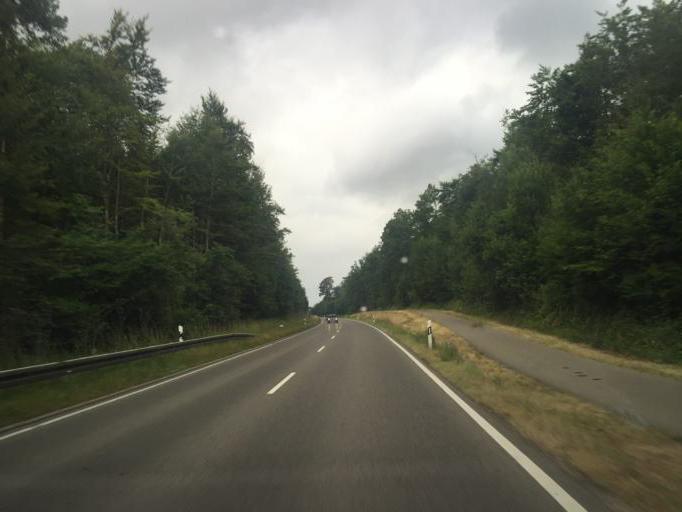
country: DE
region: Baden-Wuerttemberg
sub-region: Regierungsbezirk Stuttgart
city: Deckenpfronn
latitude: 48.6479
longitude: 8.8570
